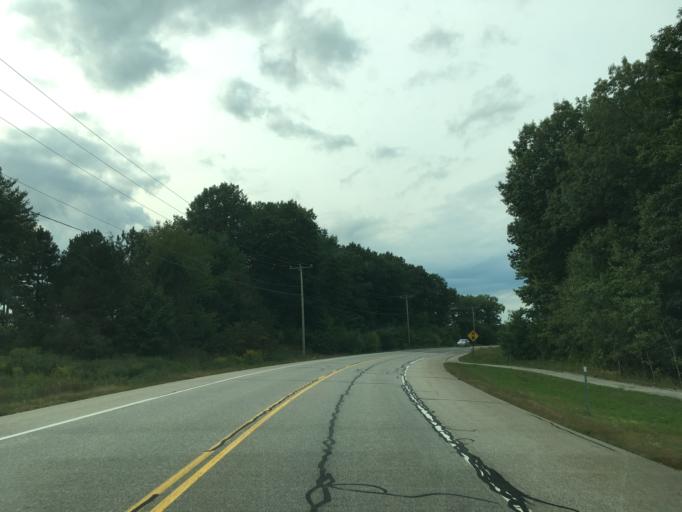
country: US
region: New Hampshire
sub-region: Rockingham County
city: Exeter
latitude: 42.9872
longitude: -70.9269
